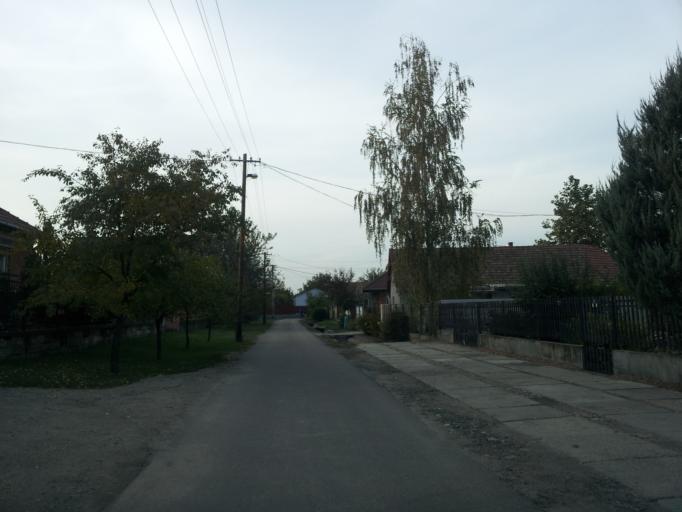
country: HU
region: Pest
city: Nagykata
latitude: 47.4175
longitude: 19.7282
